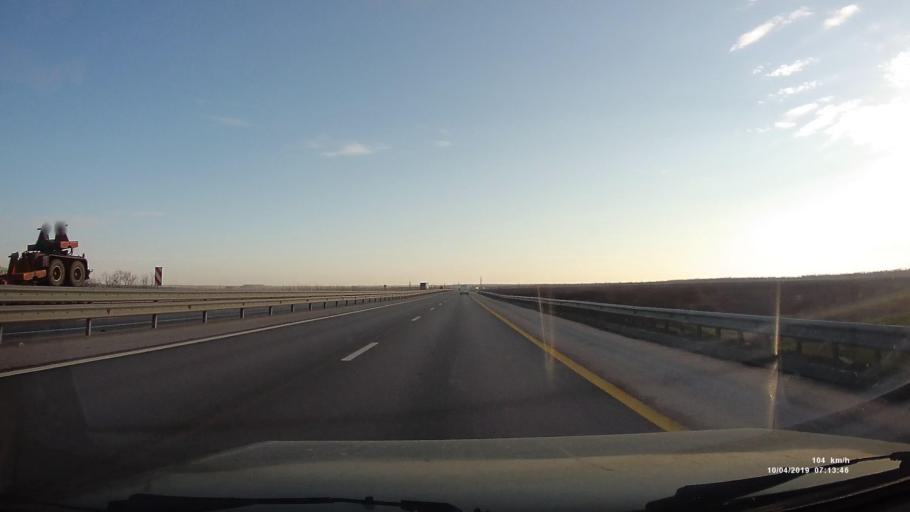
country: RU
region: Rostov
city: Ayutinskiy
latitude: 47.7405
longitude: 40.1296
